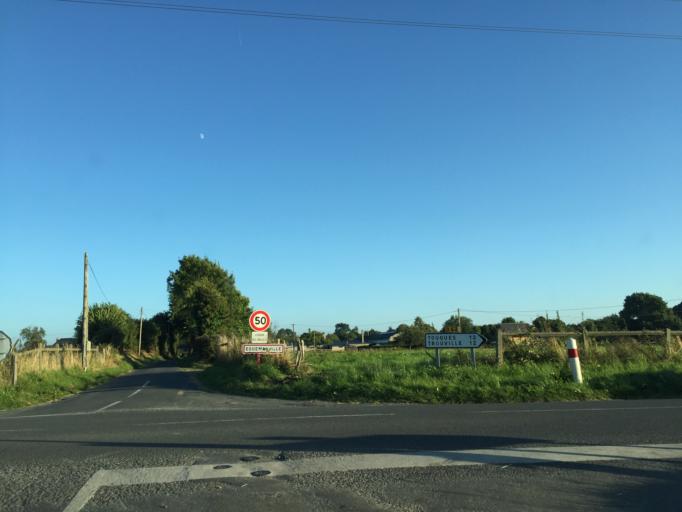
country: FR
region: Lower Normandy
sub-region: Departement du Calvados
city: Equemauville
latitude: 49.3974
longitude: 0.1986
